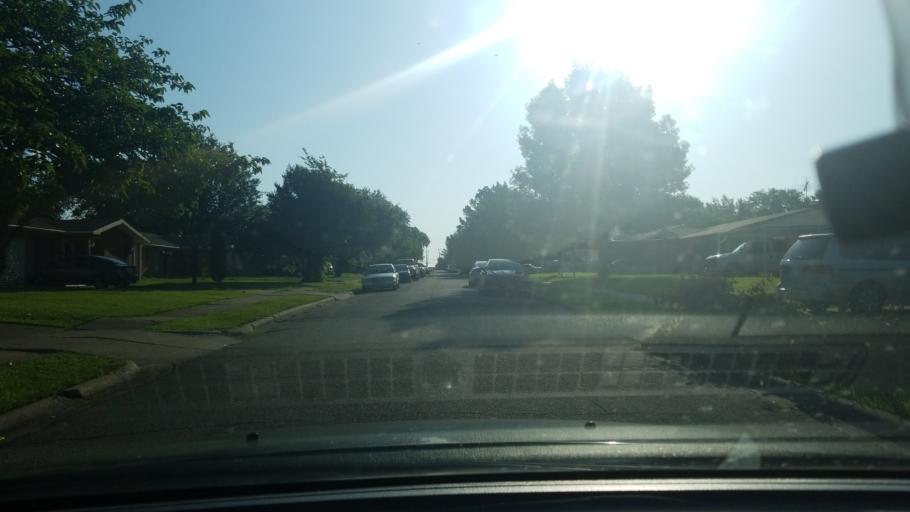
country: US
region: Texas
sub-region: Dallas County
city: Mesquite
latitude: 32.8123
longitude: -96.6418
